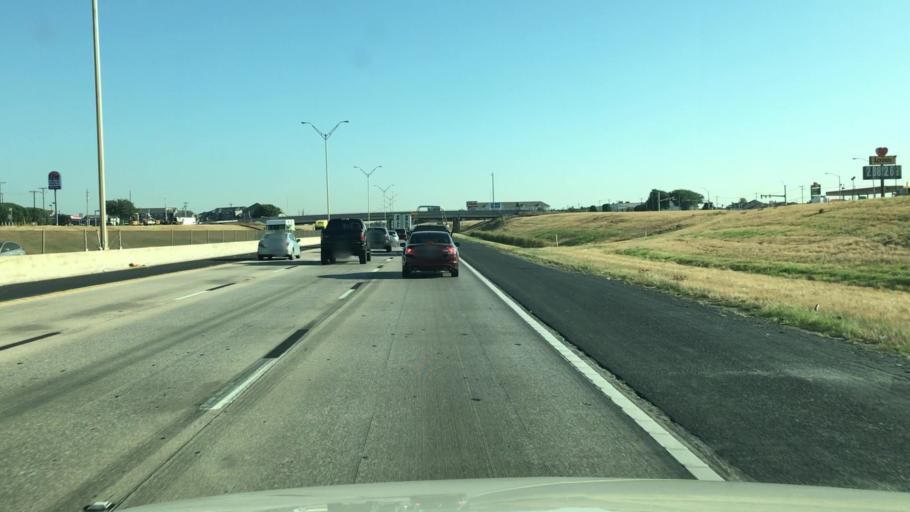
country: US
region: Texas
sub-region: Tarrant County
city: Everman
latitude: 32.5964
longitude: -97.3193
